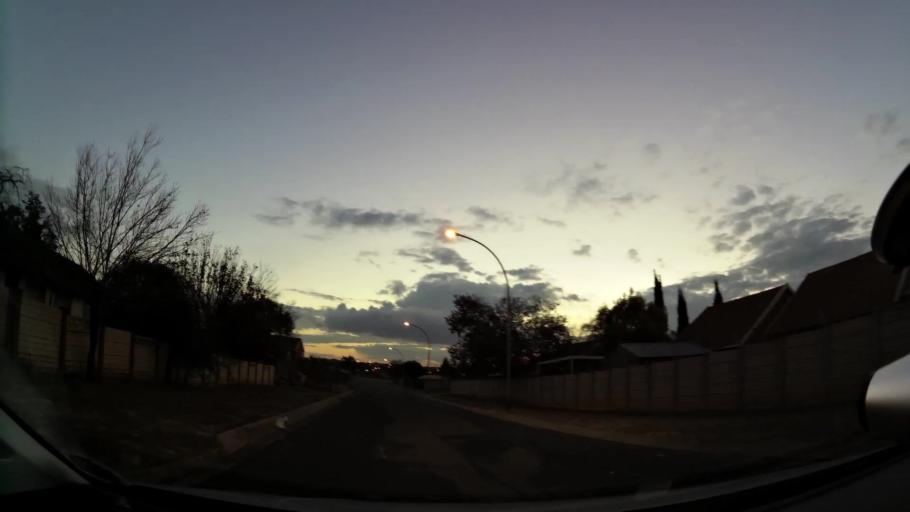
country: ZA
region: Orange Free State
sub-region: Mangaung Metropolitan Municipality
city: Bloemfontein
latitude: -29.1534
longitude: 26.1928
